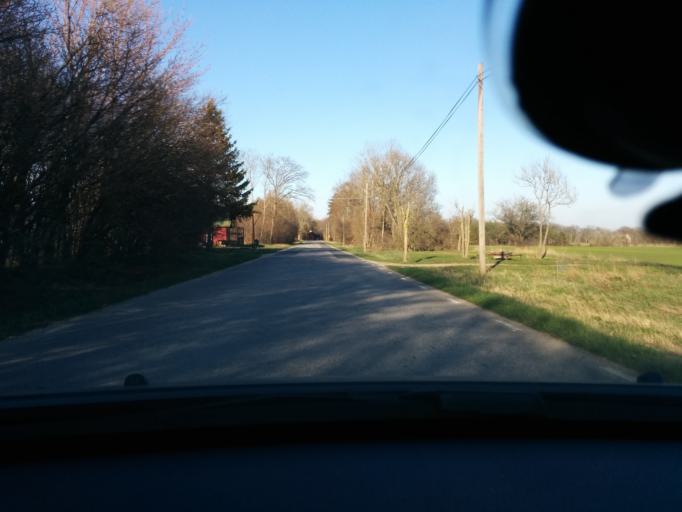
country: SE
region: Gotland
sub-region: Gotland
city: Hemse
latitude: 57.1658
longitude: 18.3719
